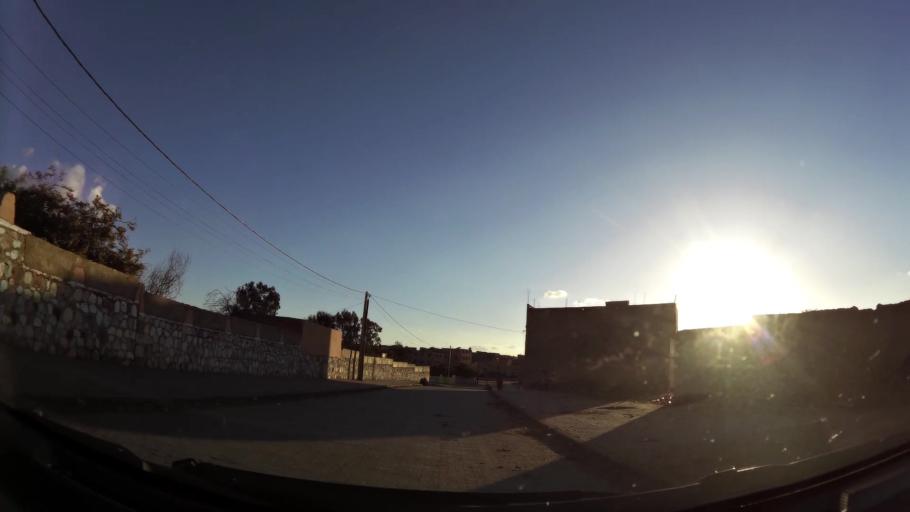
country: MA
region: Marrakech-Tensift-Al Haouz
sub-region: Kelaa-Des-Sraghna
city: Sidi Abdallah
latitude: 32.2470
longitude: -7.9481
